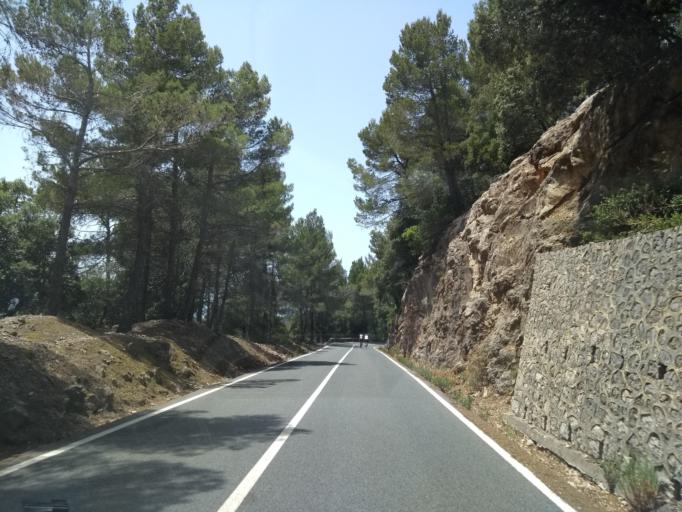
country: ES
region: Balearic Islands
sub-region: Illes Balears
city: Fornalutx
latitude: 39.7962
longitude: 2.7691
